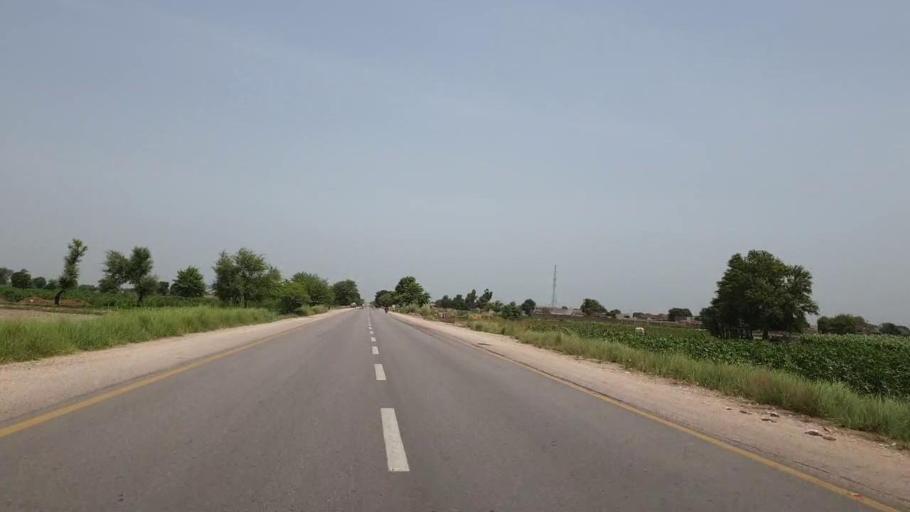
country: PK
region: Sindh
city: Shahpur Chakar
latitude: 26.1537
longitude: 68.6345
